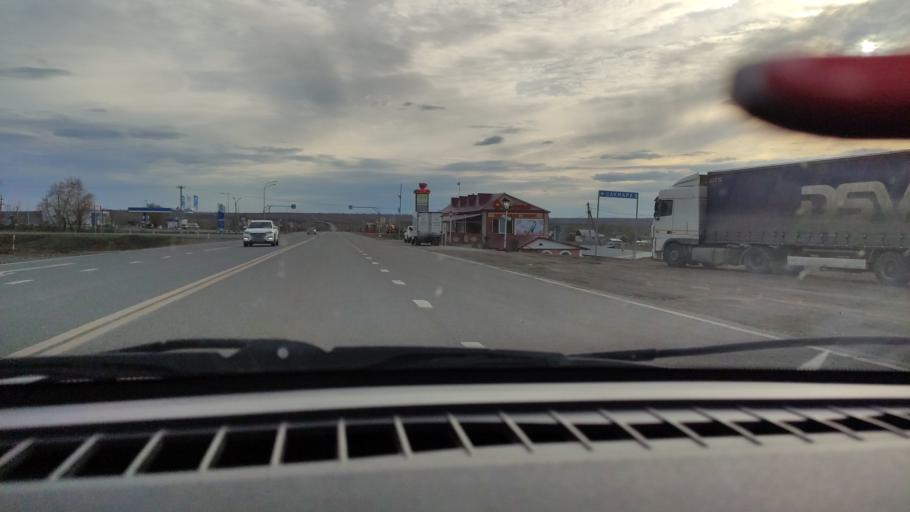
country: RU
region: Orenburg
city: Tatarskaya Kargala
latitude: 52.0283
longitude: 55.2329
